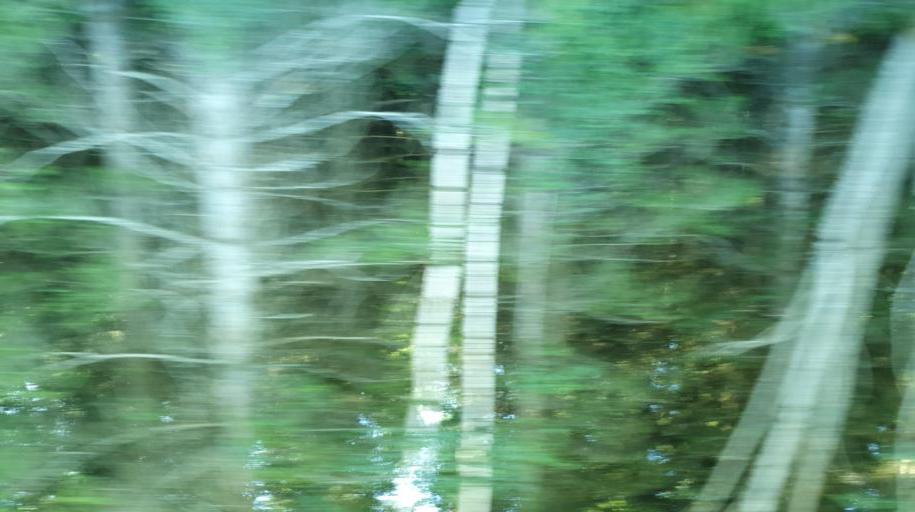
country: NO
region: Nord-Trondelag
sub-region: Levanger
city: Levanger
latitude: 63.6968
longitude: 11.2668
